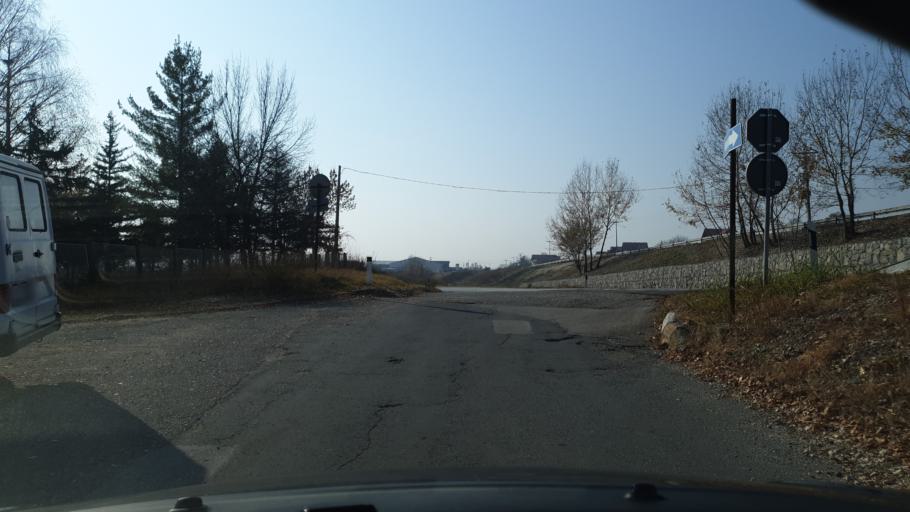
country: RS
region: Central Serbia
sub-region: Zajecarski Okrug
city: Zajecar
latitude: 43.9246
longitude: 22.2963
